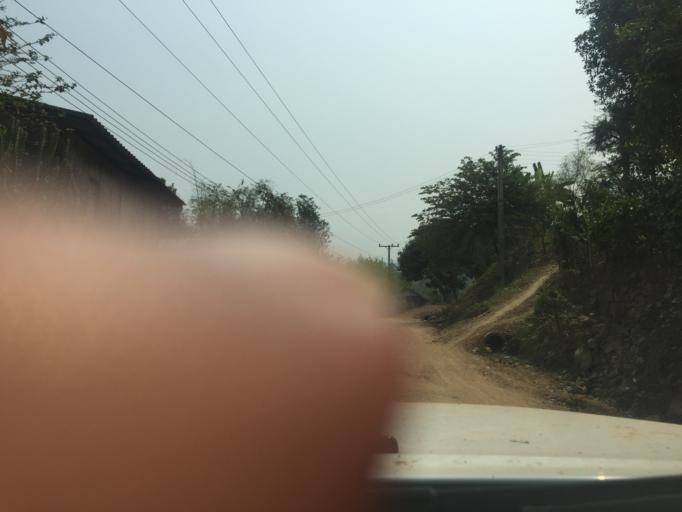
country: LA
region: Loungnamtha
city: Muang Nale
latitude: 20.3034
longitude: 101.6454
